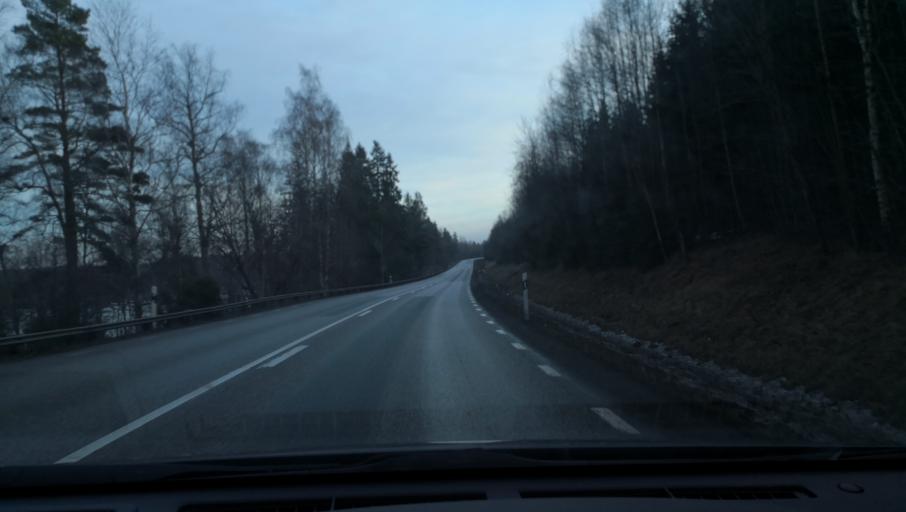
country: SE
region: OErebro
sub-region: Degerfors Kommun
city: Degerfors
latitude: 59.1211
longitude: 14.5282
